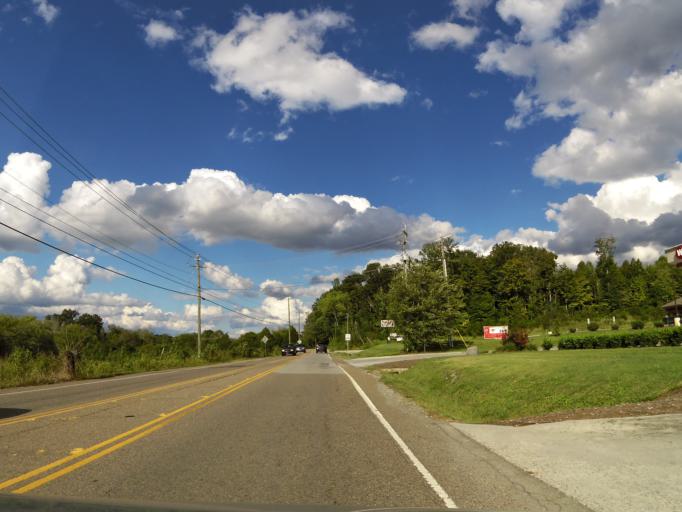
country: US
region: Tennessee
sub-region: Knox County
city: Knoxville
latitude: 36.0523
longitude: -83.8747
